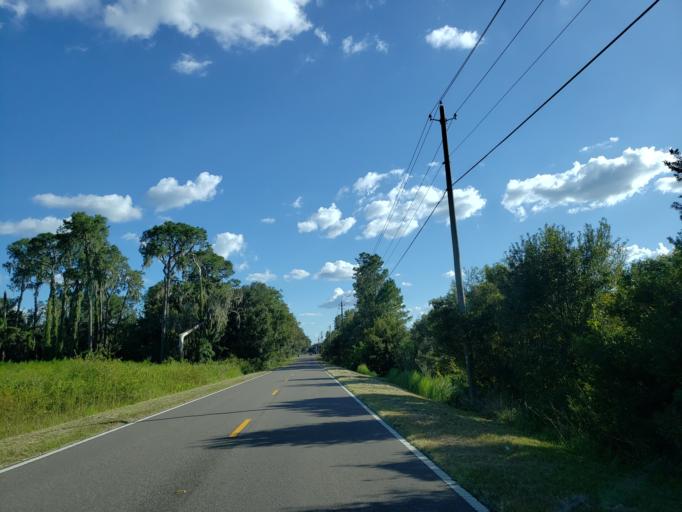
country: US
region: Florida
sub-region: Hillsborough County
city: Valrico
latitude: 27.9609
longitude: -82.2197
